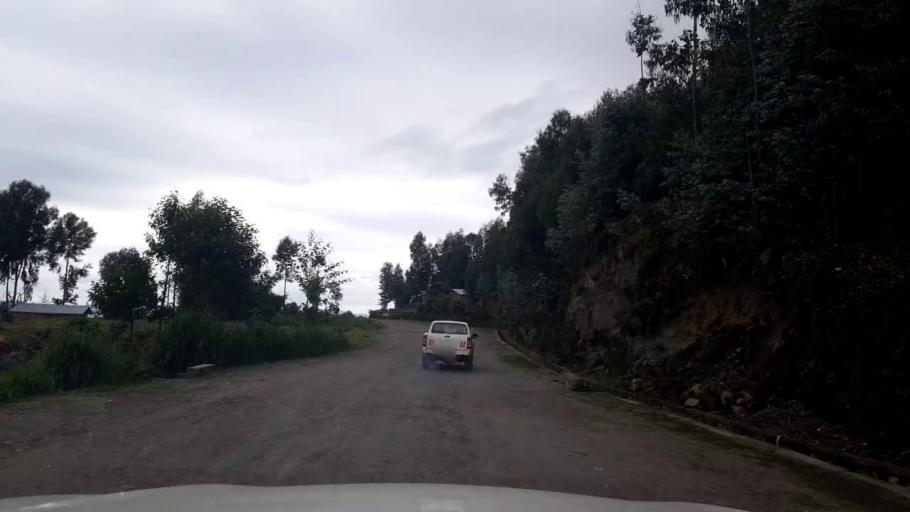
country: RW
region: Northern Province
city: Musanze
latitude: -1.4989
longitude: 29.5340
